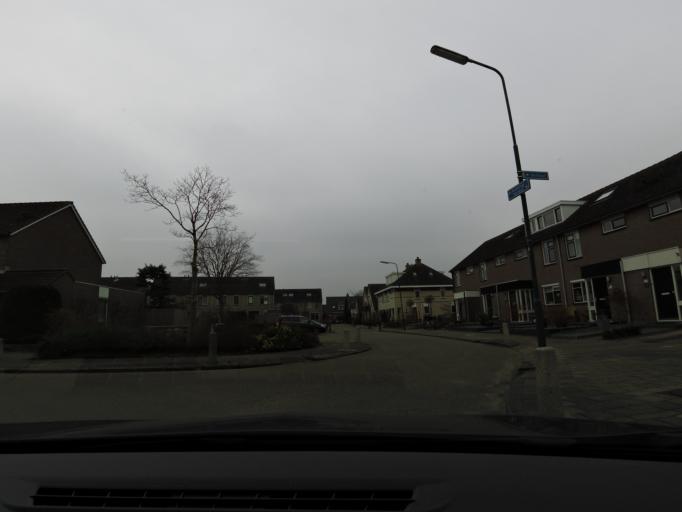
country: NL
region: Utrecht
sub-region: Gemeente Woerden
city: Woerden
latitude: 52.1100
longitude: 4.8906
